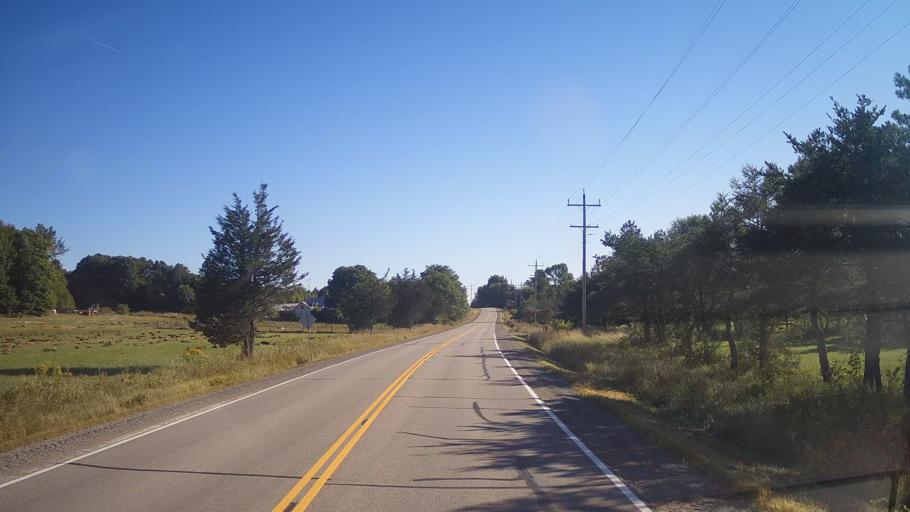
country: CA
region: Ontario
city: Gananoque
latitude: 44.5881
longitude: -76.1041
